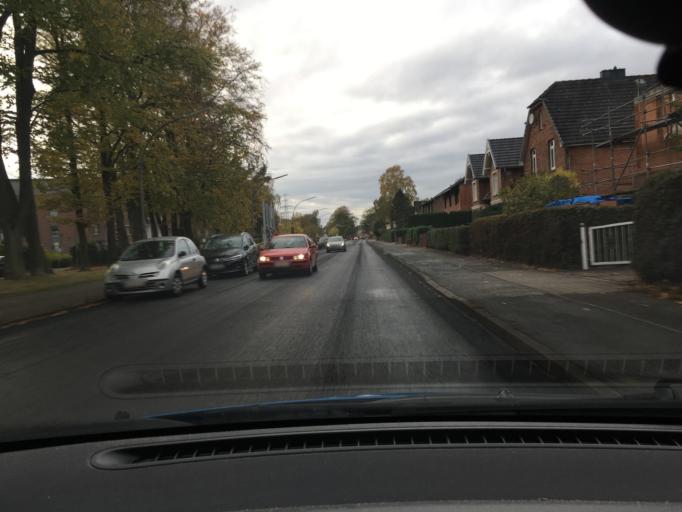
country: DE
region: Schleswig-Holstein
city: Wentorf bei Hamburg
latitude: 53.4911
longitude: 10.2604
